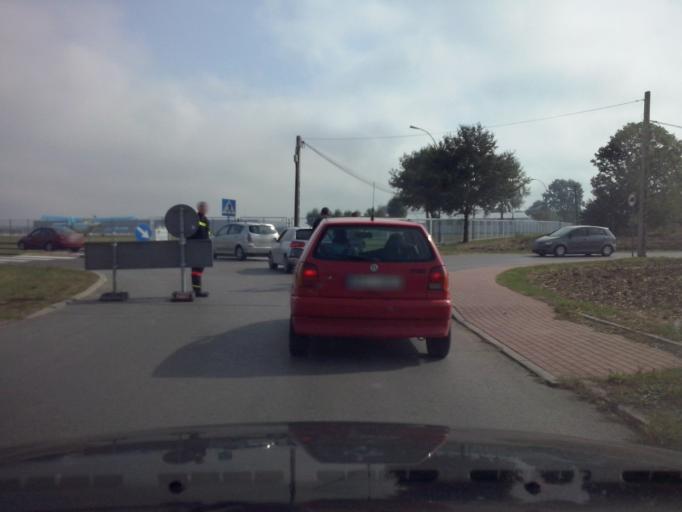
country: PL
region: Subcarpathian Voivodeship
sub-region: Powiat mielecki
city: Mielec
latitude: 50.3170
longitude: 21.4410
